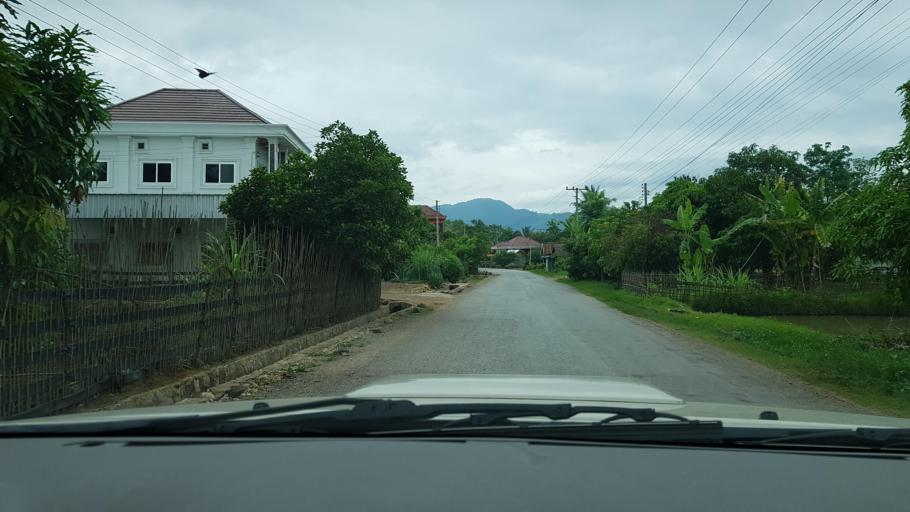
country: LA
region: Loungnamtha
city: Muang Nale
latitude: 20.2831
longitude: 101.6143
